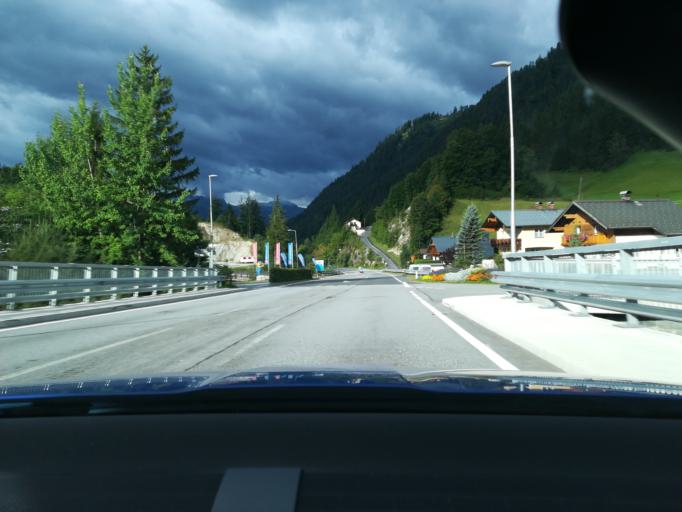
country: AT
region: Salzburg
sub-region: Politischer Bezirk Hallein
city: Abtenau
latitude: 47.5898
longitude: 13.4638
